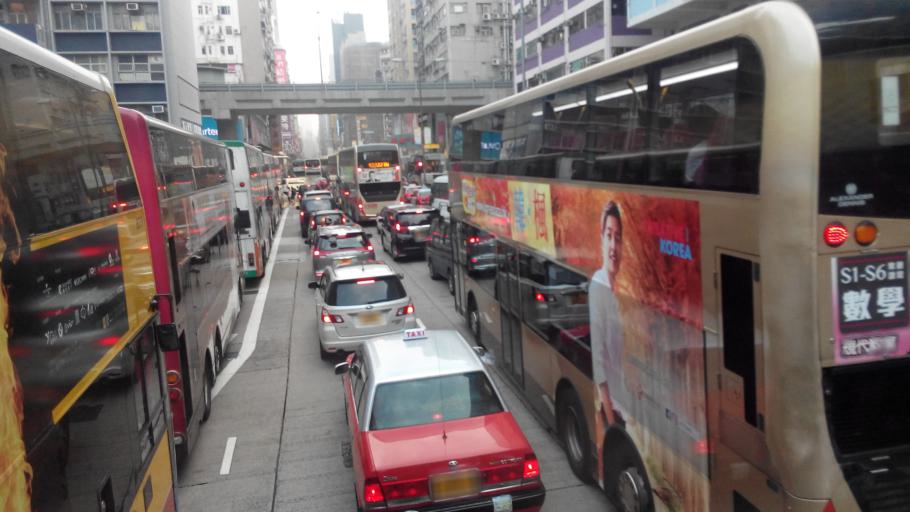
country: HK
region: Sham Shui Po
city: Sham Shui Po
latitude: 22.3247
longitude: 114.1684
